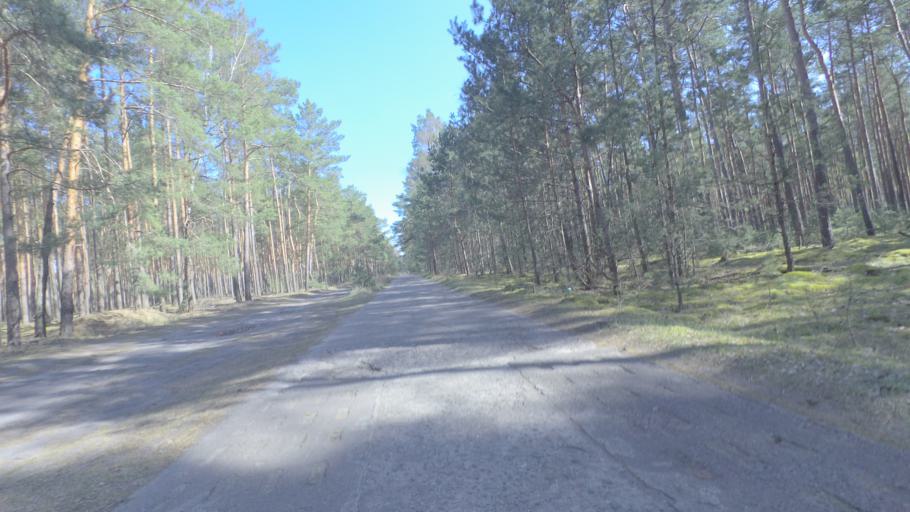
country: DE
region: Brandenburg
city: Halbe
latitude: 52.1734
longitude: 13.7446
